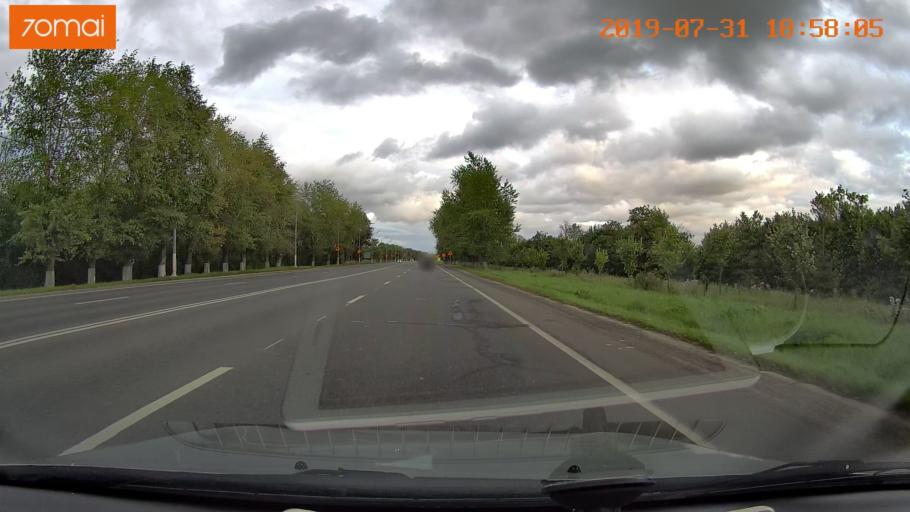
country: RU
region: Moskovskaya
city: Raduzhnyy
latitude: 55.1493
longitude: 38.7000
